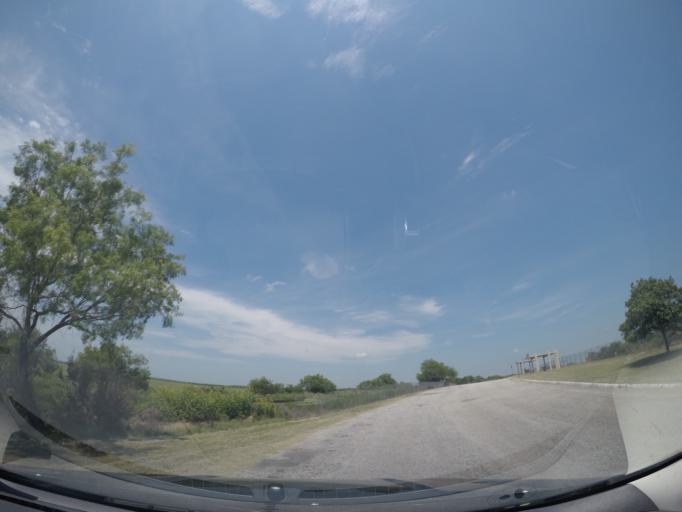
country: US
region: Texas
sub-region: Uvalde County
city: Sabinal
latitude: 29.3177
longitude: -99.5664
